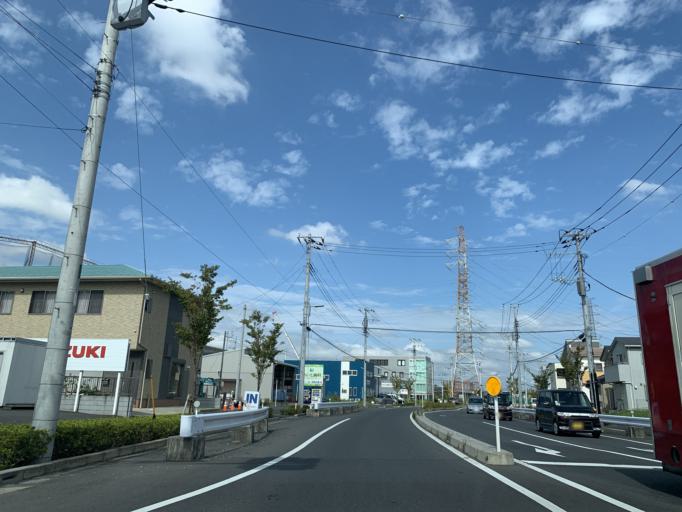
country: JP
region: Chiba
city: Nagareyama
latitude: 35.8595
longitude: 139.9167
